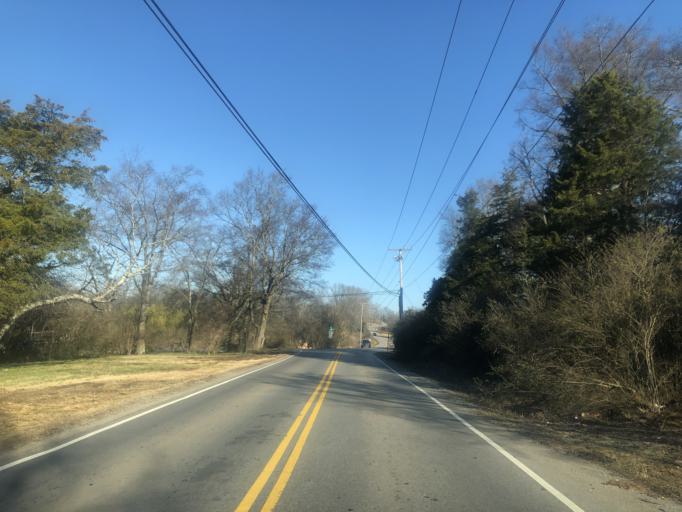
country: US
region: Tennessee
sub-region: Williamson County
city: Nolensville
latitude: 36.0102
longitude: -86.6655
